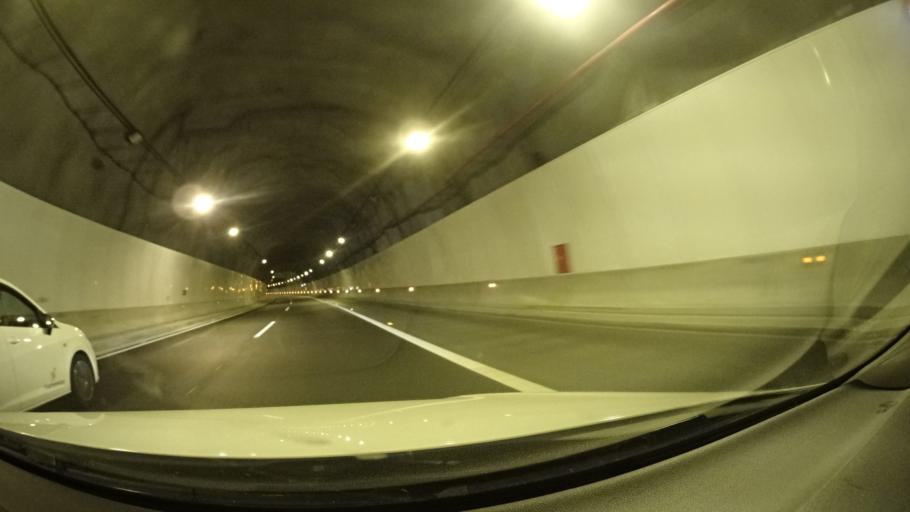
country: ES
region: Canary Islands
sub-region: Provincia de Las Palmas
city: Puerto Rico
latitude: 27.8084
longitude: -15.7133
